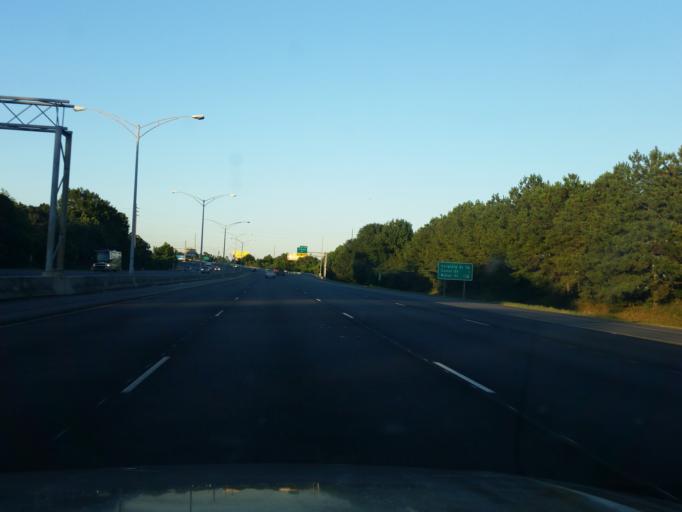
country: US
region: Alabama
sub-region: Mobile County
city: Mobile
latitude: 30.6632
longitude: -88.0547
